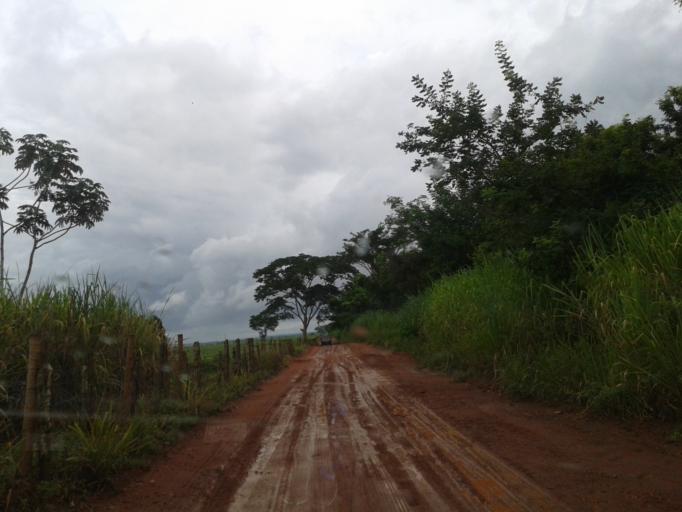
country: BR
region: Minas Gerais
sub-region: Santa Vitoria
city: Santa Vitoria
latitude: -18.7040
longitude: -49.9595
